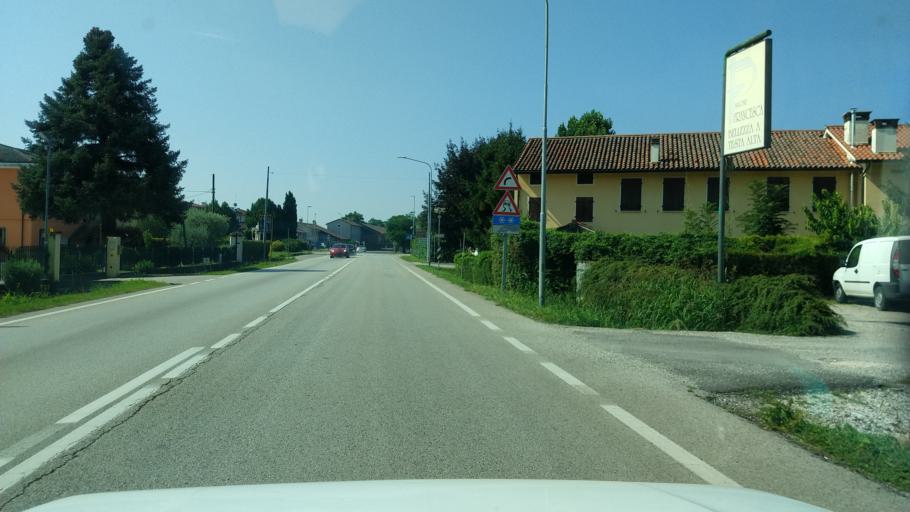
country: IT
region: Veneto
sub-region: Provincia di Vicenza
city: Bressanvido
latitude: 45.6656
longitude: 11.6353
